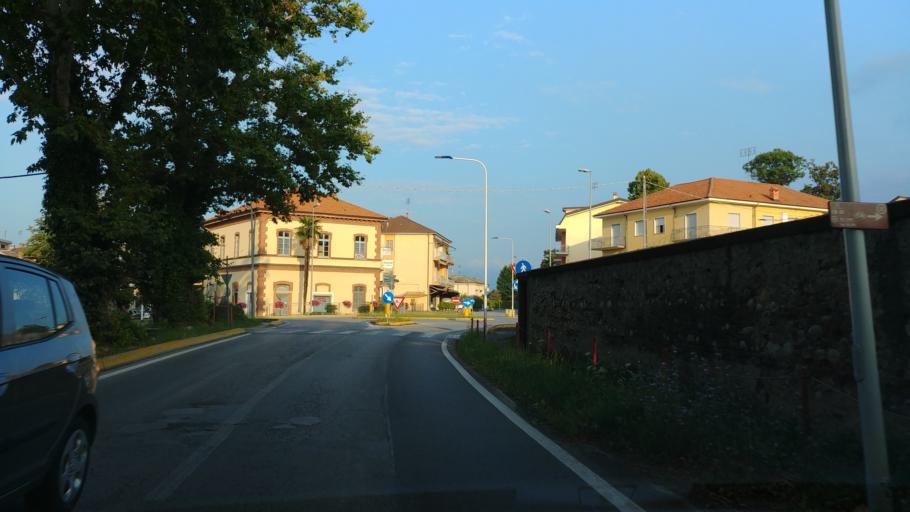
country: IT
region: Piedmont
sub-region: Provincia di Cuneo
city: Cuneo
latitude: 44.3787
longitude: 7.5716
